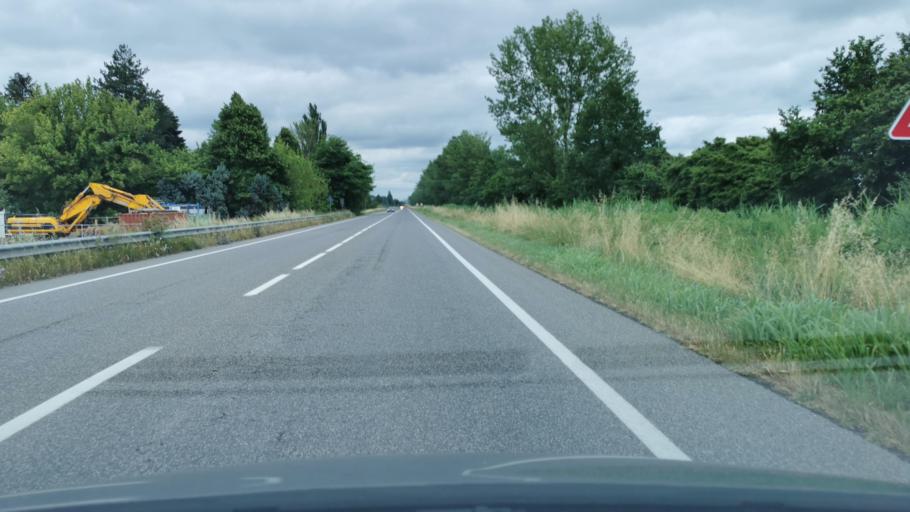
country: IT
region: Emilia-Romagna
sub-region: Provincia di Ravenna
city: Cotignola
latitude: 44.3859
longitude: 11.9534
